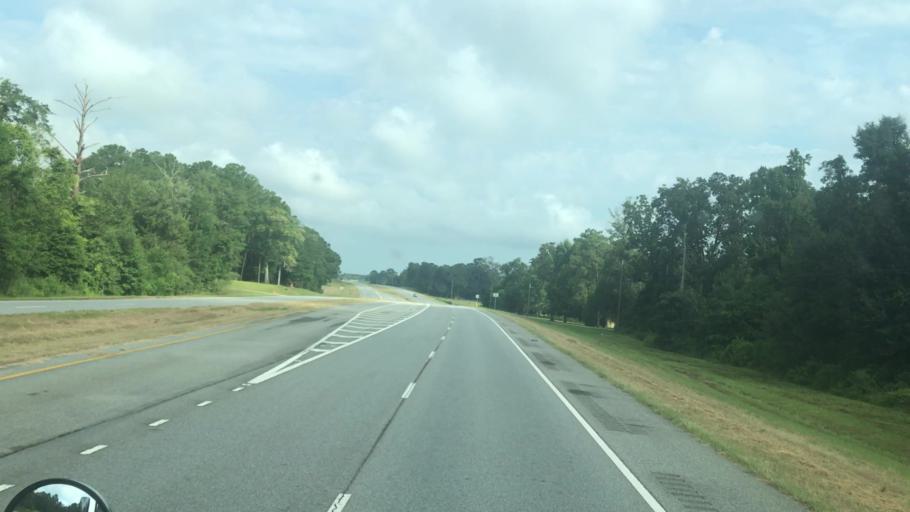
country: US
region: Georgia
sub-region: Miller County
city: Colquitt
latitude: 31.2450
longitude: -84.7916
